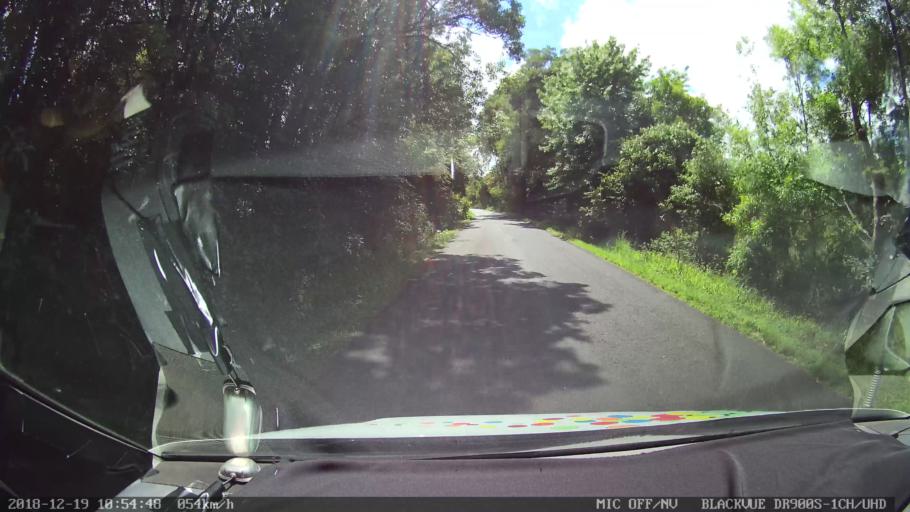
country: AU
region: New South Wales
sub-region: Lismore Municipality
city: Nimbin
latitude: -28.5939
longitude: 153.2487
